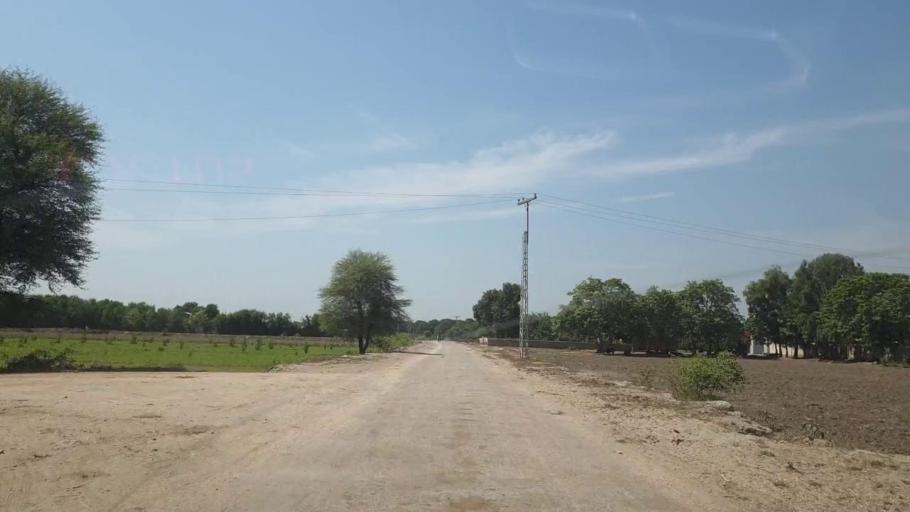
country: PK
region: Sindh
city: Tando Allahyar
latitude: 25.4071
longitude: 68.6461
